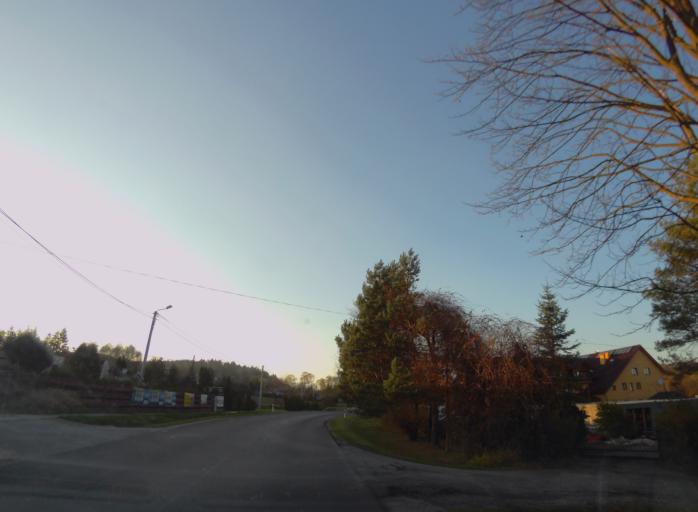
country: PL
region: Subcarpathian Voivodeship
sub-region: Powiat leski
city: Polanczyk
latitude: 49.3912
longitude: 22.3900
